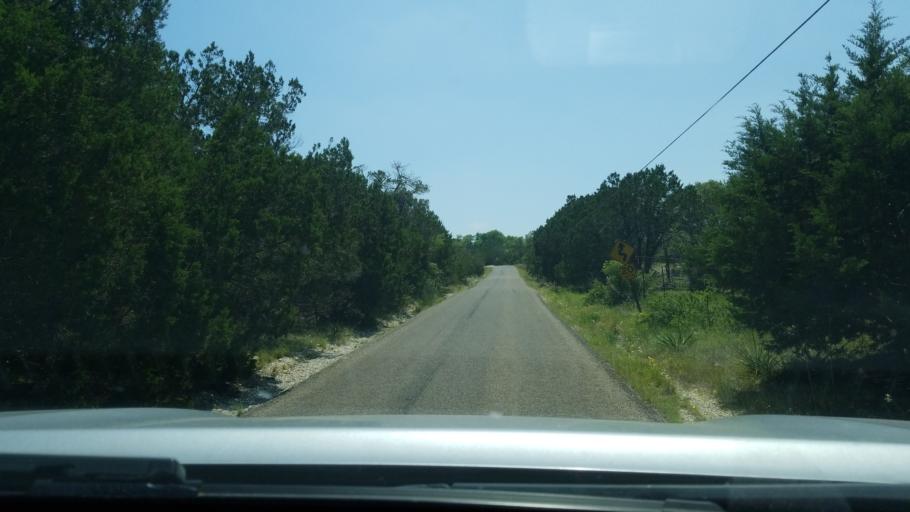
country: US
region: Texas
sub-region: Blanco County
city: Blanco
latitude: 30.0832
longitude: -98.4006
